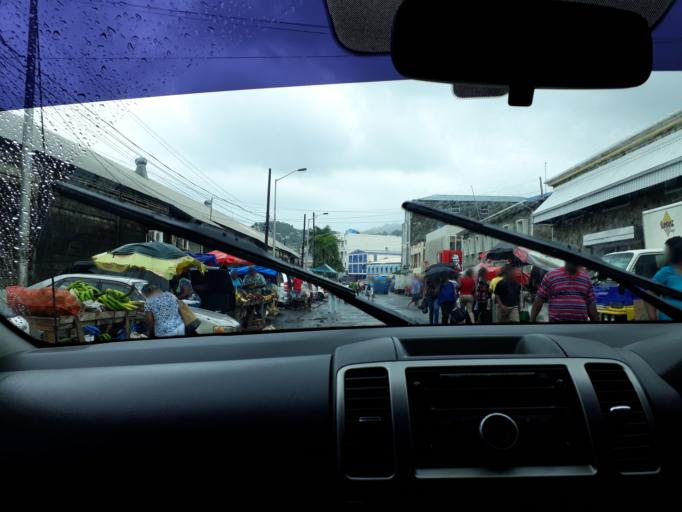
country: VC
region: Saint George
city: Kingstown
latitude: 13.1517
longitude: -61.2234
